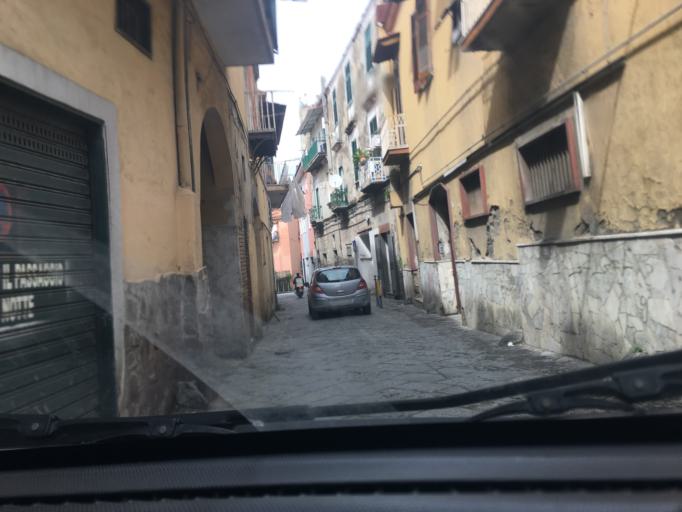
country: IT
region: Campania
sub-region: Provincia di Napoli
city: Calvizzano
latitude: 40.8958
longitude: 14.1872
